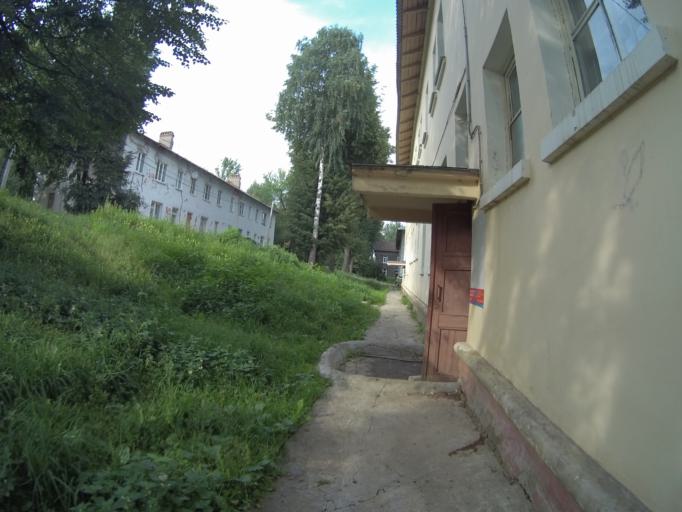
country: RU
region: Vladimir
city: Kommunar
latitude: 56.1447
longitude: 40.4329
